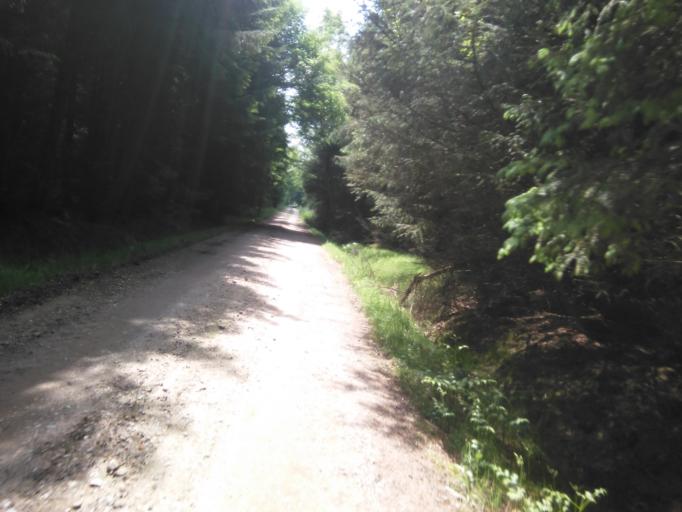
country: DK
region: Central Jutland
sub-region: Favrskov Kommune
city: Hammel
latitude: 56.2644
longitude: 9.9367
